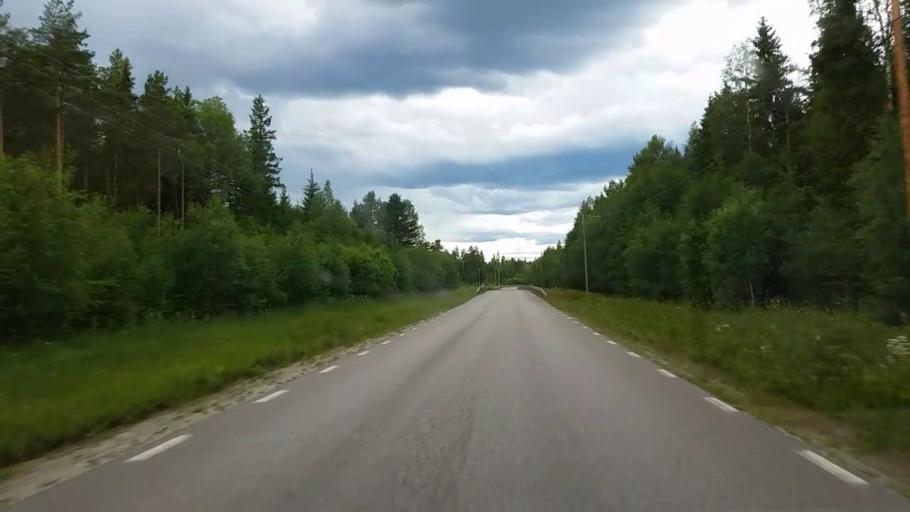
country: SE
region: Gaevleborg
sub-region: Ovanakers Kommun
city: Edsbyn
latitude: 61.4546
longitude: 15.8776
